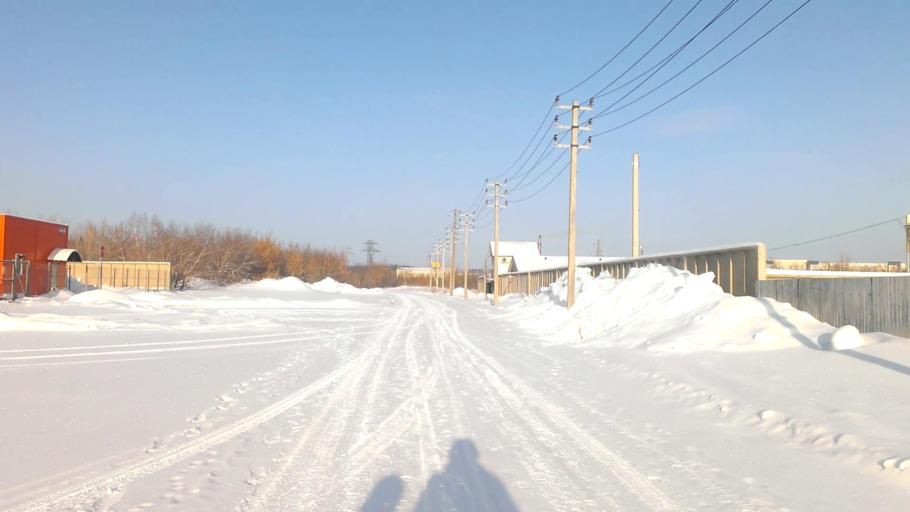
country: RU
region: Altai Krai
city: Novosilikatnyy
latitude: 53.3434
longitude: 83.6298
